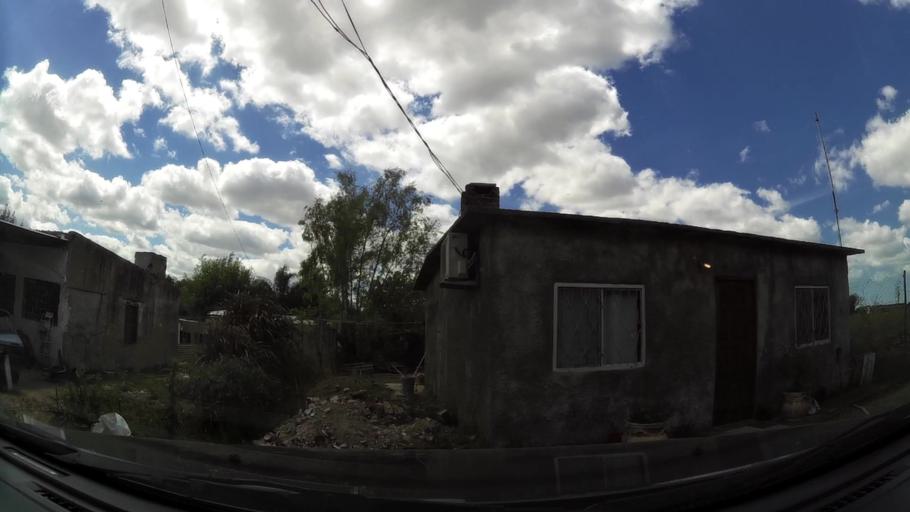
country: UY
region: Canelones
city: Colonia Nicolich
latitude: -34.8170
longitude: -56.0413
